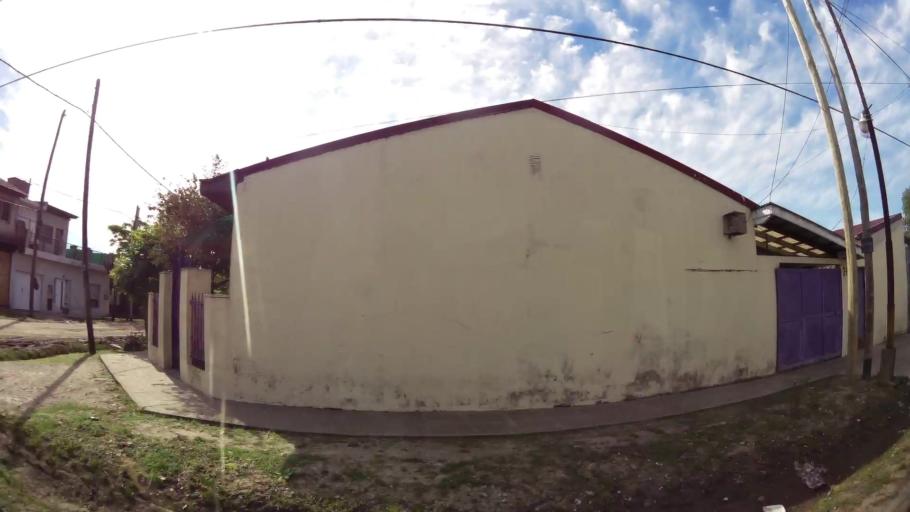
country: AR
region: Buenos Aires
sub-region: Partido de Quilmes
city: Quilmes
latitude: -34.7812
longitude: -58.3027
